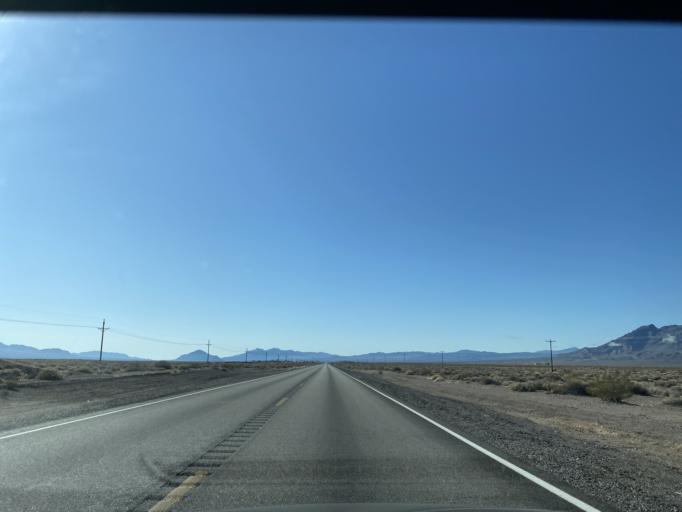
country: US
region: Nevada
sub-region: Nye County
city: Pahrump
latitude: 36.4434
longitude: -116.4220
